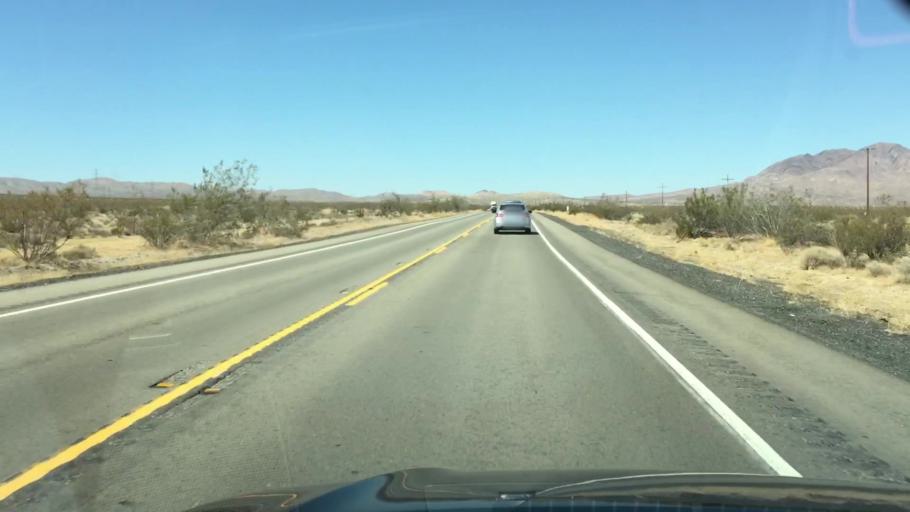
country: US
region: California
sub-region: Kern County
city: Boron
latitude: 35.2628
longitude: -117.6133
